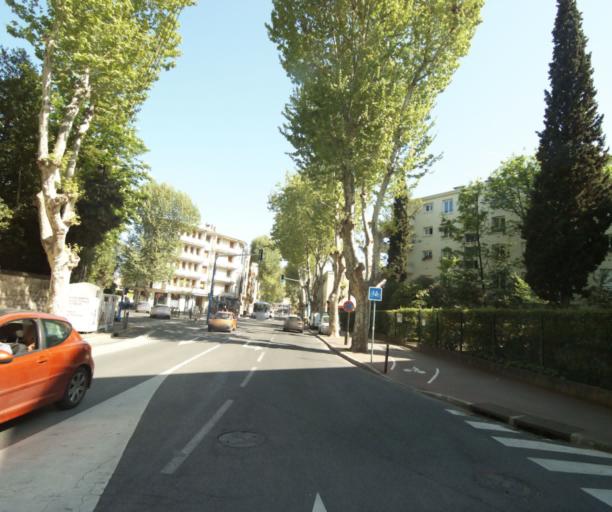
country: FR
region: Languedoc-Roussillon
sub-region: Departement de l'Herault
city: Montpellier
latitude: 43.6139
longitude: 3.8658
